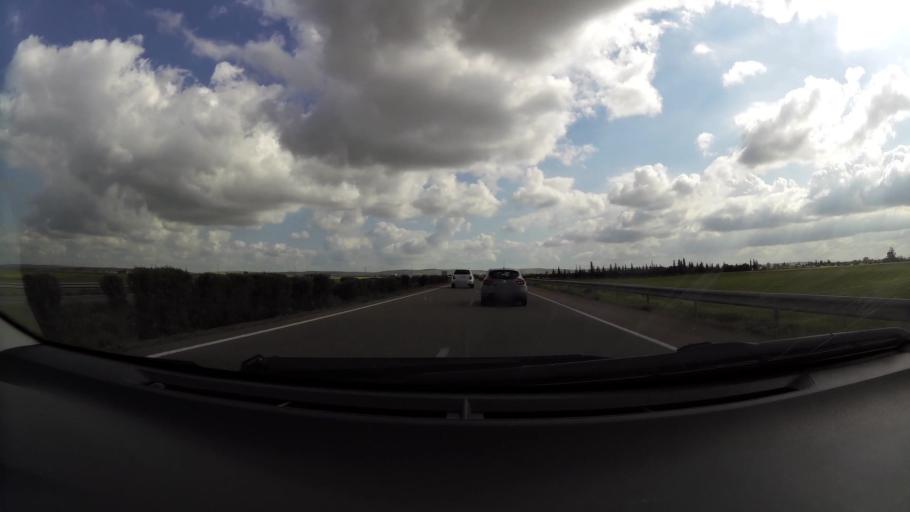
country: MA
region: Chaouia-Ouardigha
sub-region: Settat Province
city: Berrechid
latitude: 33.1321
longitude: -7.5780
